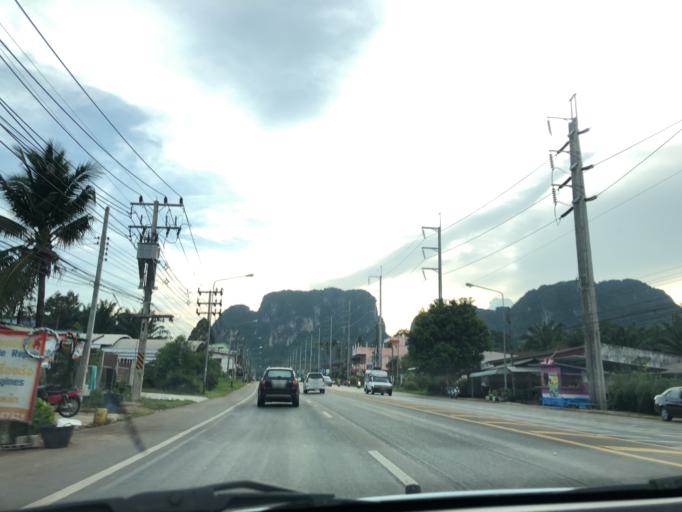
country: TH
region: Krabi
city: Krabi
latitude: 8.0831
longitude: 98.8665
